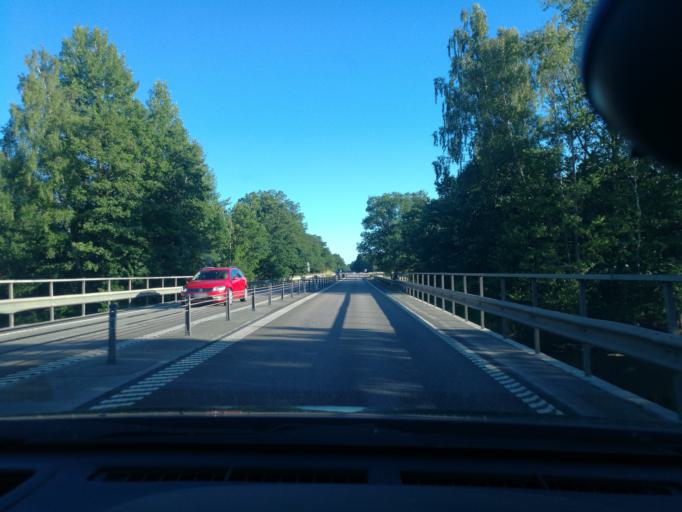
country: SE
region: Kalmar
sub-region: Monsteras Kommun
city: Timmernabben
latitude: 56.9566
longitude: 16.3905
